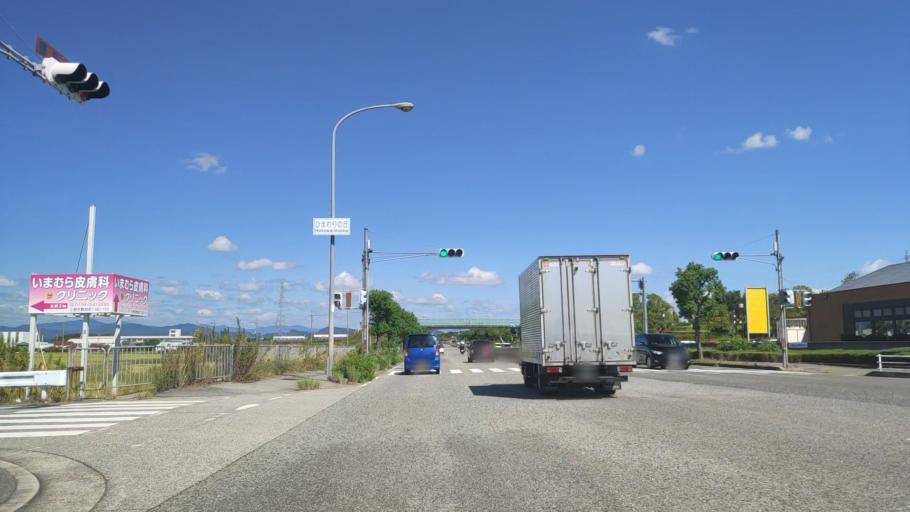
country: JP
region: Hyogo
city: Ono
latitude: 34.8678
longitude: 134.9522
